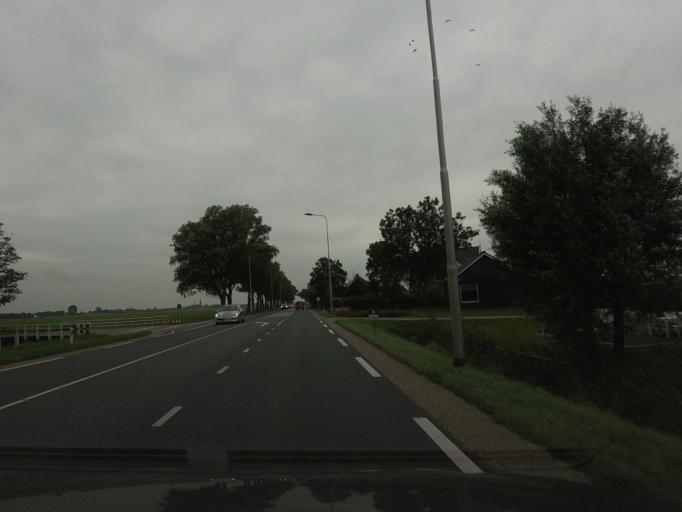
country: NL
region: North Holland
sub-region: Gemeente Opmeer
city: Opmeer
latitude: 52.6961
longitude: 4.9917
